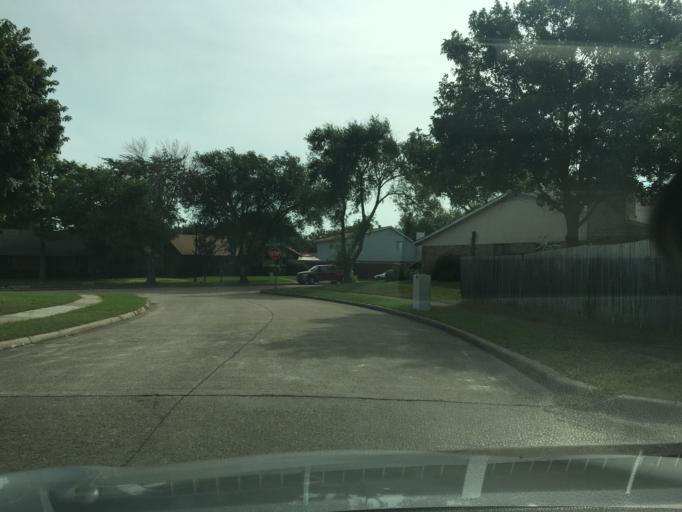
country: US
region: Texas
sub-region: Dallas County
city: Richardson
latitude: 32.9641
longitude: -96.6778
